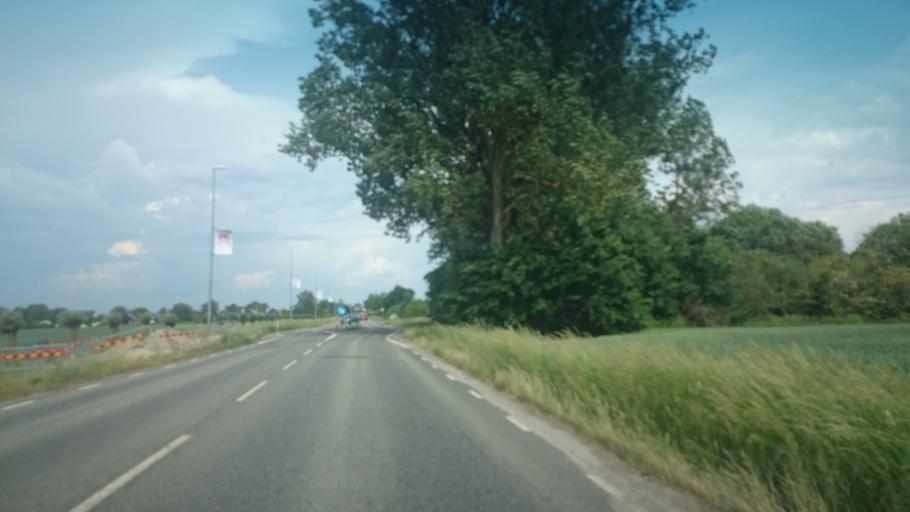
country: SE
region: Skane
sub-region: Kristianstads Kommun
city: Norra Asum
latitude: 56.0047
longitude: 14.1513
